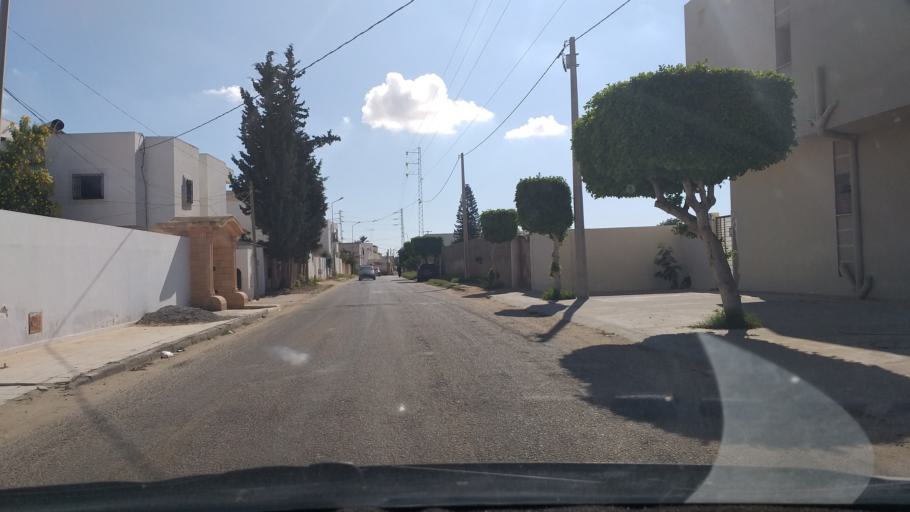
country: TN
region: Safaqis
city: Al Qarmadah
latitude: 34.8011
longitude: 10.7731
